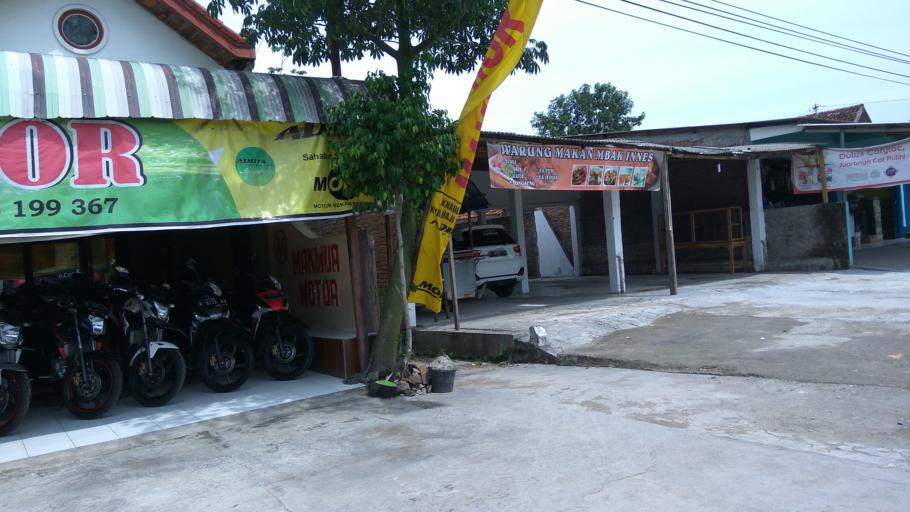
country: ID
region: Central Java
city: Mranggen
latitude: -7.0615
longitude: 110.6668
